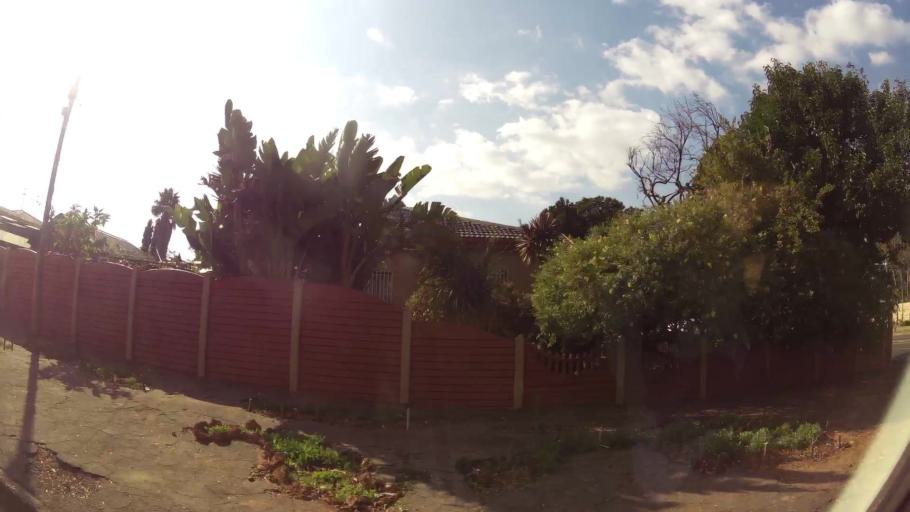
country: ZA
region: Gauteng
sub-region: Ekurhuleni Metropolitan Municipality
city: Germiston
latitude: -26.1800
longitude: 28.1813
